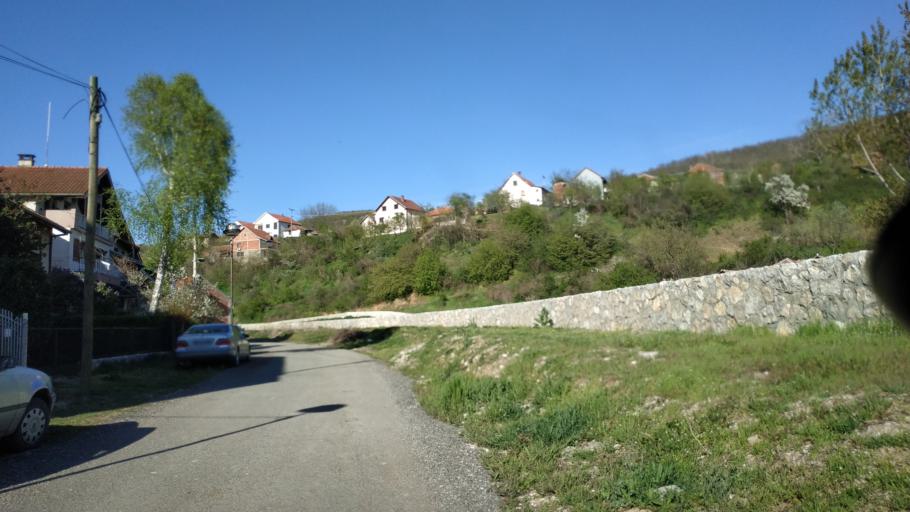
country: RS
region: Central Serbia
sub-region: Nisavski Okrug
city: Aleksinac
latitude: 43.5441
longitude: 21.7132
